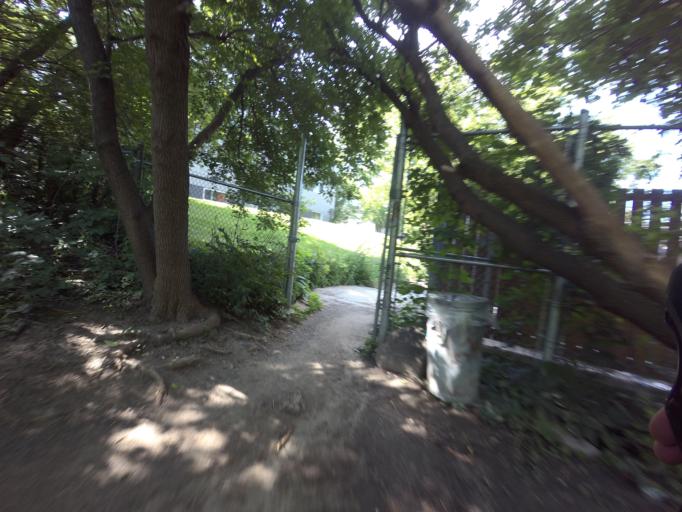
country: CA
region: Ontario
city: Bells Corners
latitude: 45.3518
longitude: -75.7668
